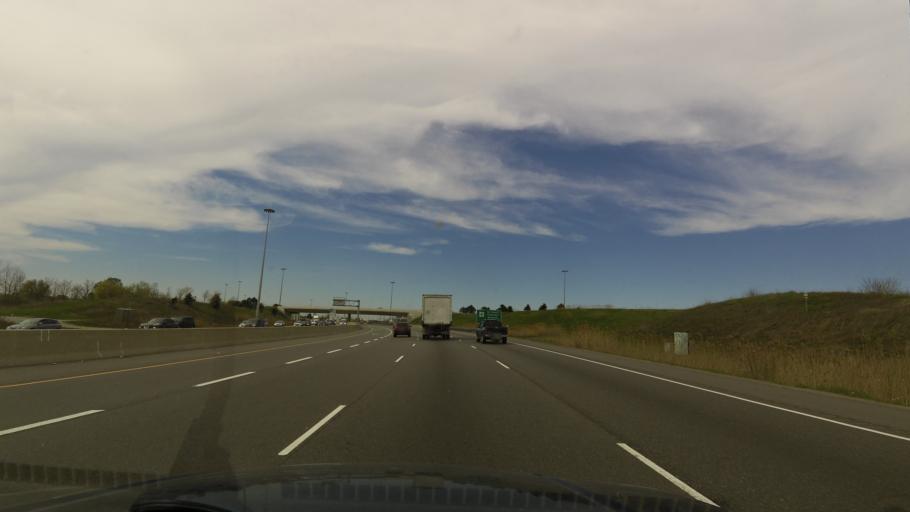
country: CA
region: Ontario
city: Mississauga
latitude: 43.6157
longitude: -79.6316
